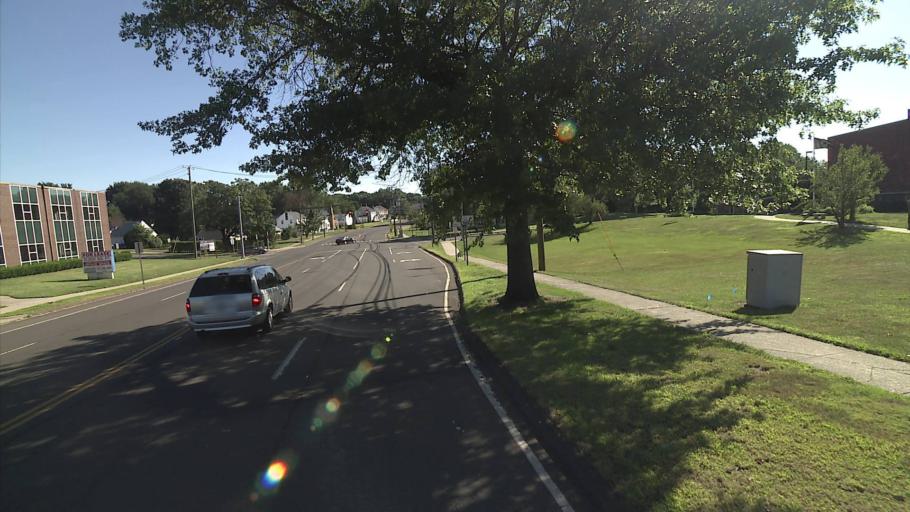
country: US
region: Connecticut
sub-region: New Haven County
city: Hamden
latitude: 41.3805
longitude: -72.9130
